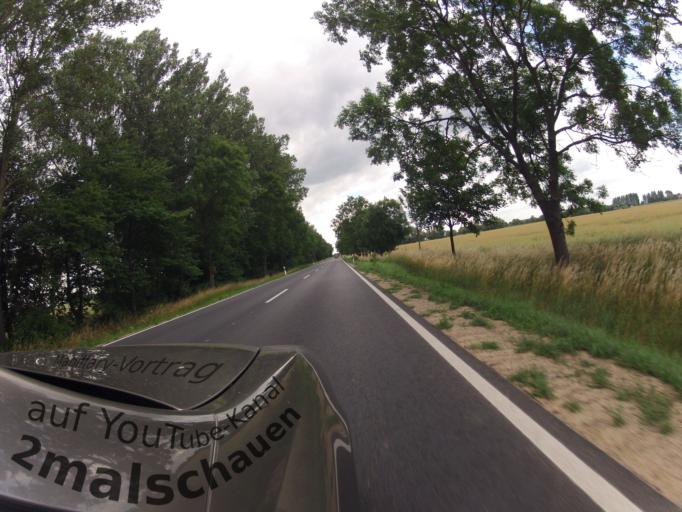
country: DE
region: Mecklenburg-Vorpommern
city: Ducherow
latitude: 53.7994
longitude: 13.7412
